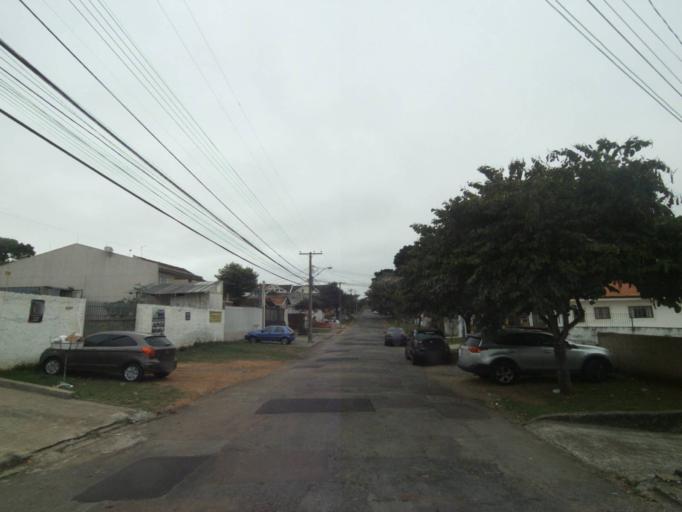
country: BR
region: Parana
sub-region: Curitiba
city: Curitiba
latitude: -25.4732
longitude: -49.2781
